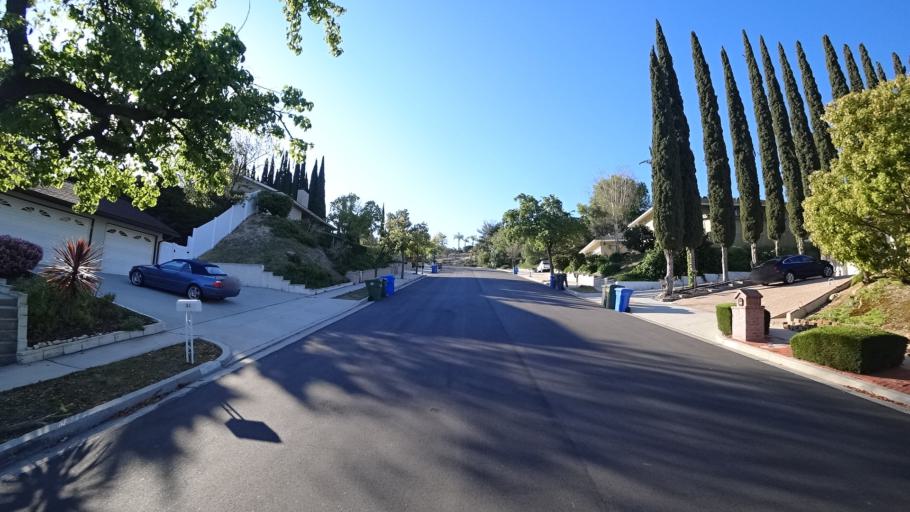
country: US
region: California
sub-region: Ventura County
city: Thousand Oaks
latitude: 34.1881
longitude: -118.8406
